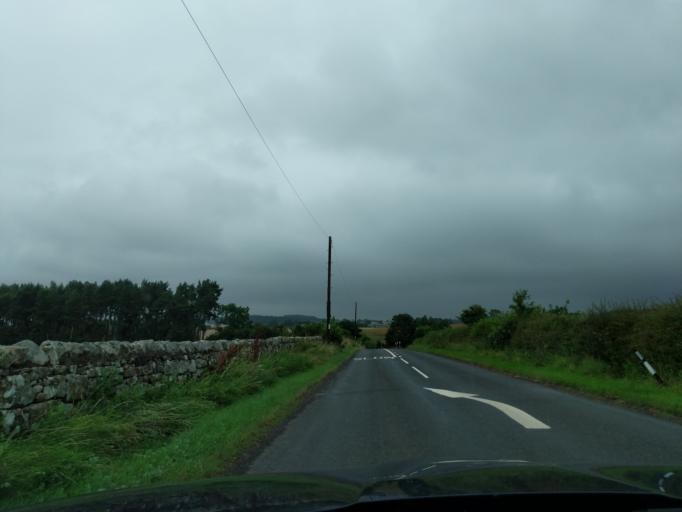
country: GB
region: England
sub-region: Northumberland
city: Ford
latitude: 55.6619
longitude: -2.1055
